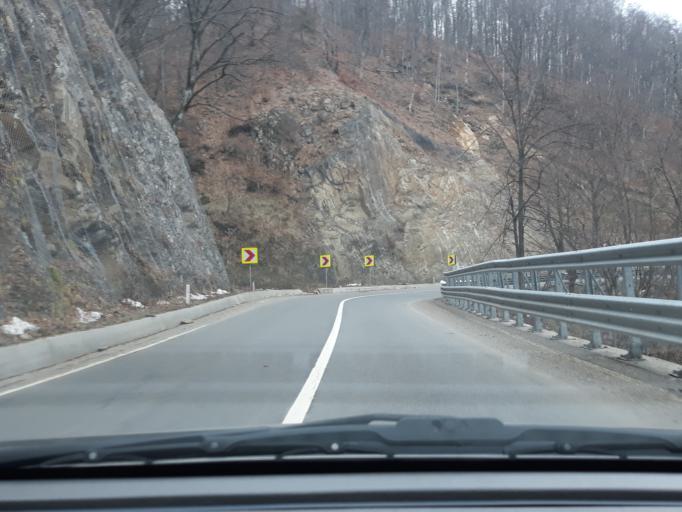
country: RO
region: Bihor
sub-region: Oras Alesd
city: Padurea Neagra
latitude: 47.1192
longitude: 22.4103
